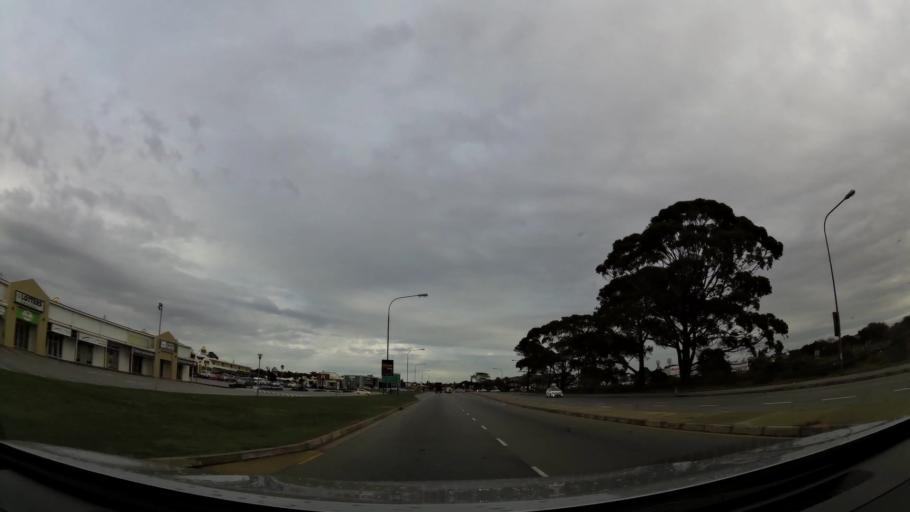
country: ZA
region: Eastern Cape
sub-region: Nelson Mandela Bay Metropolitan Municipality
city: Port Elizabeth
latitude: -33.9910
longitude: 25.5541
